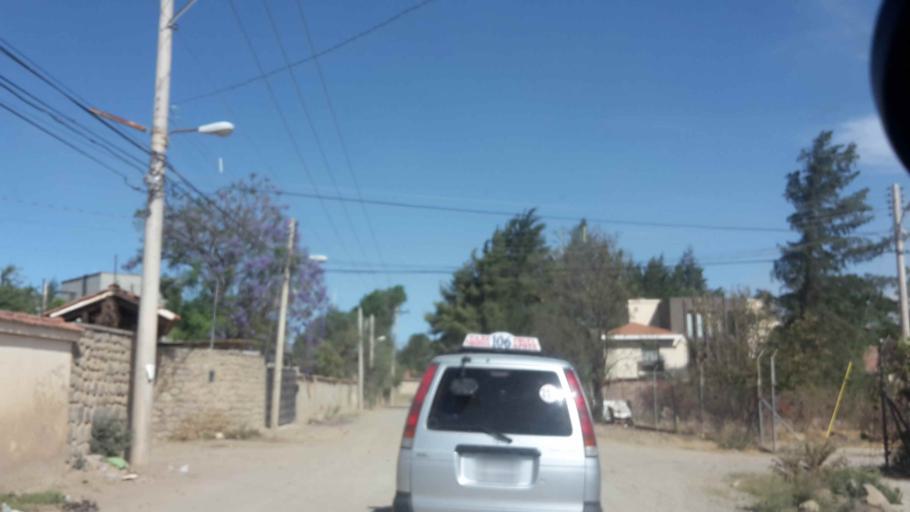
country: BO
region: Cochabamba
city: Cochabamba
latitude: -17.3393
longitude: -66.2072
